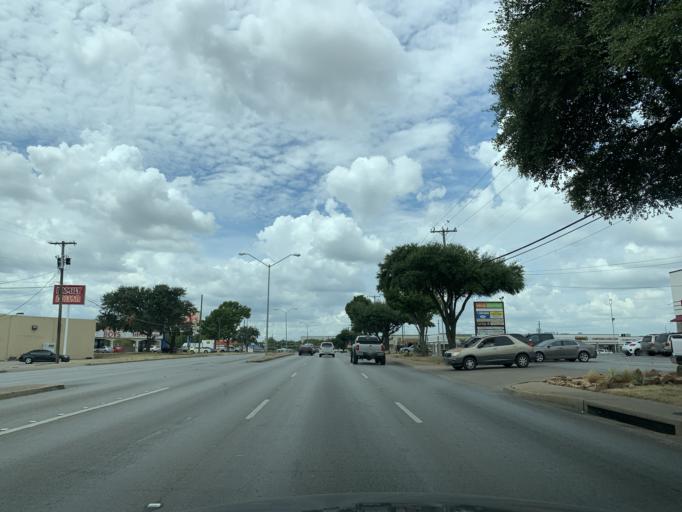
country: US
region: Texas
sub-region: Dallas County
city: Cockrell Hill
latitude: 32.7551
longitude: -96.8711
